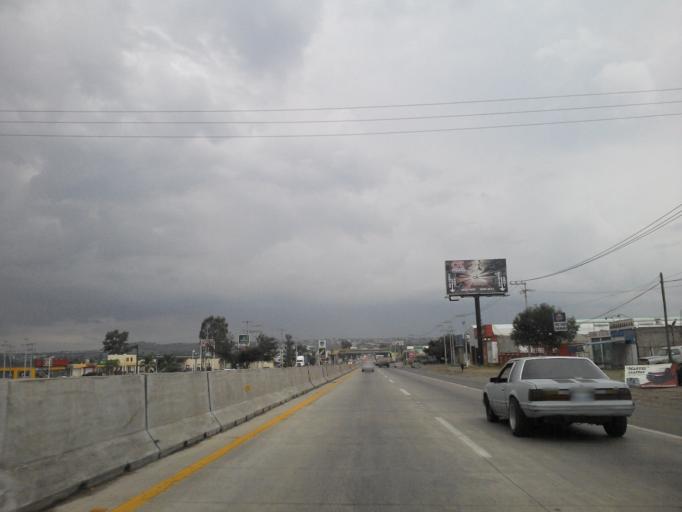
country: MX
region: Jalisco
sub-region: Tonala
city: Colonia Guadalupana
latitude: 20.5841
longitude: -103.2206
